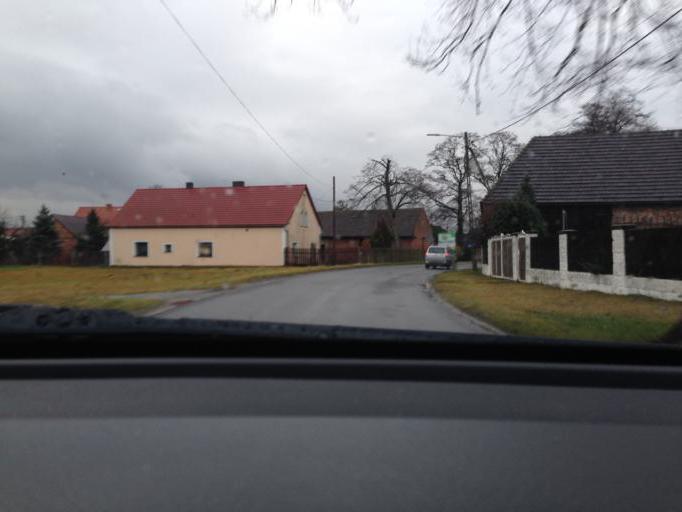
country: PL
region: Opole Voivodeship
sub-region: Powiat opolski
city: Chrzastowice
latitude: 50.7255
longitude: 18.0744
